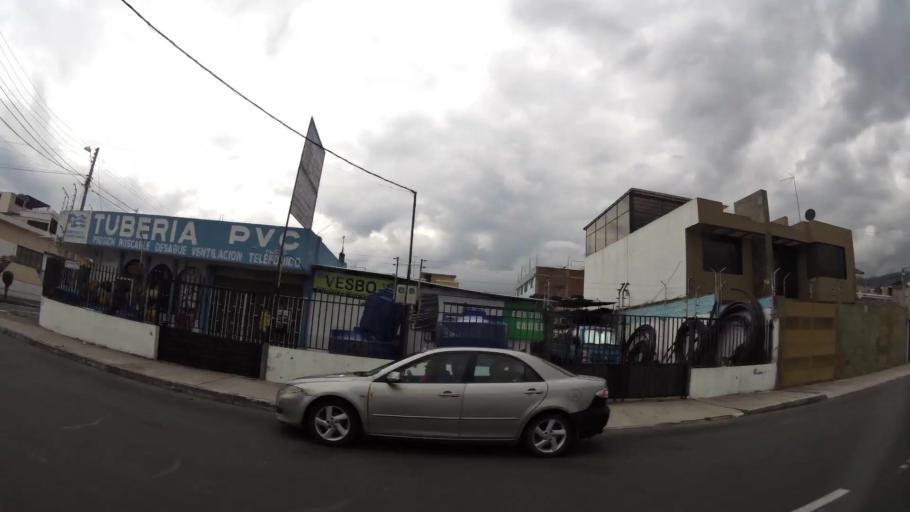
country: EC
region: Tungurahua
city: Ambato
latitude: -1.2371
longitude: -78.6133
